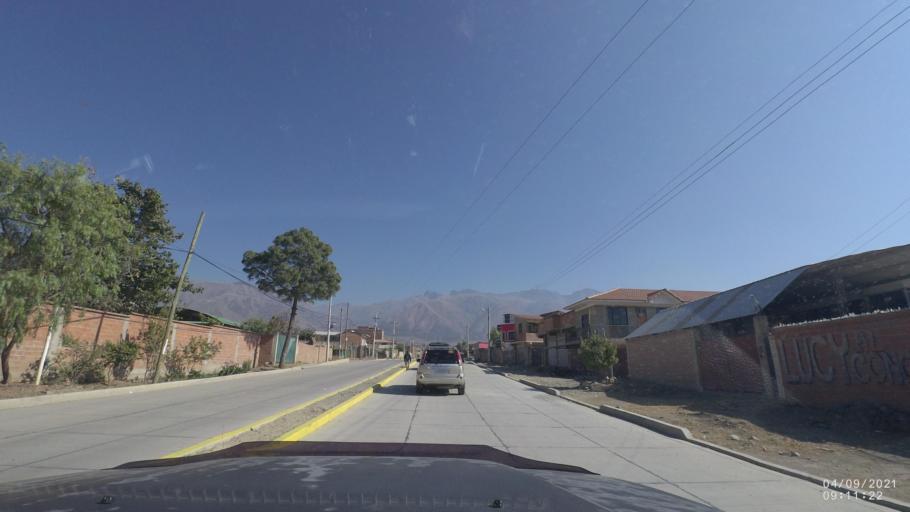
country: BO
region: Cochabamba
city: Sipe Sipe
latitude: -17.3895
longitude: -66.3353
